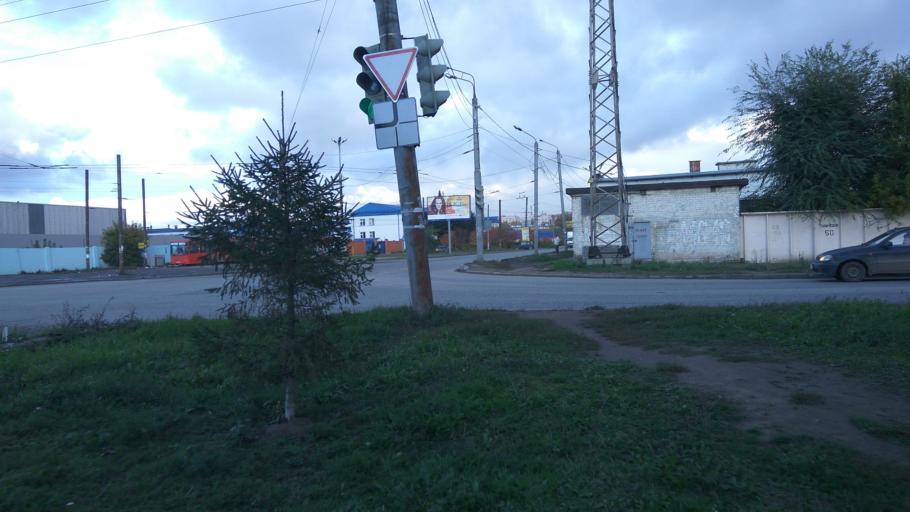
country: RU
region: Tatarstan
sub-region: Gorod Kazan'
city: Kazan
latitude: 55.7332
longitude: 49.1340
